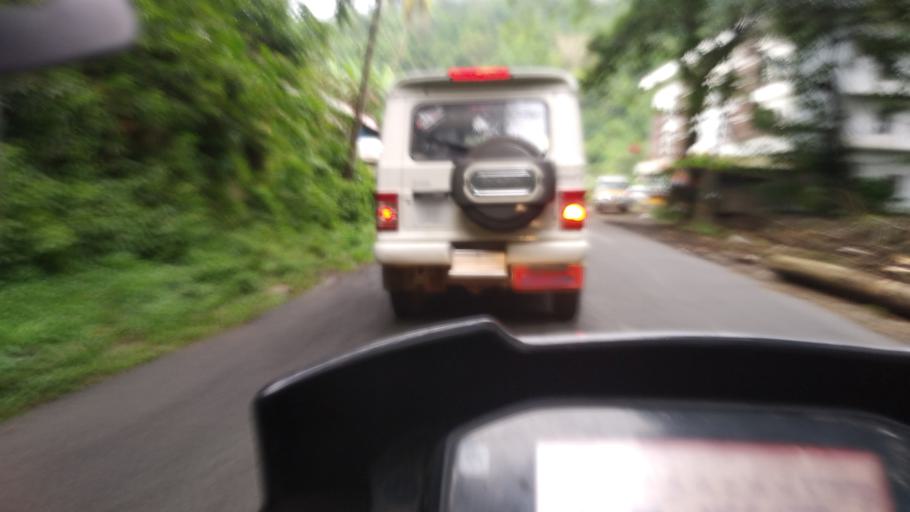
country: IN
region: Kerala
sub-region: Idukki
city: Kuttampuzha
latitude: 10.0631
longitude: 76.7750
